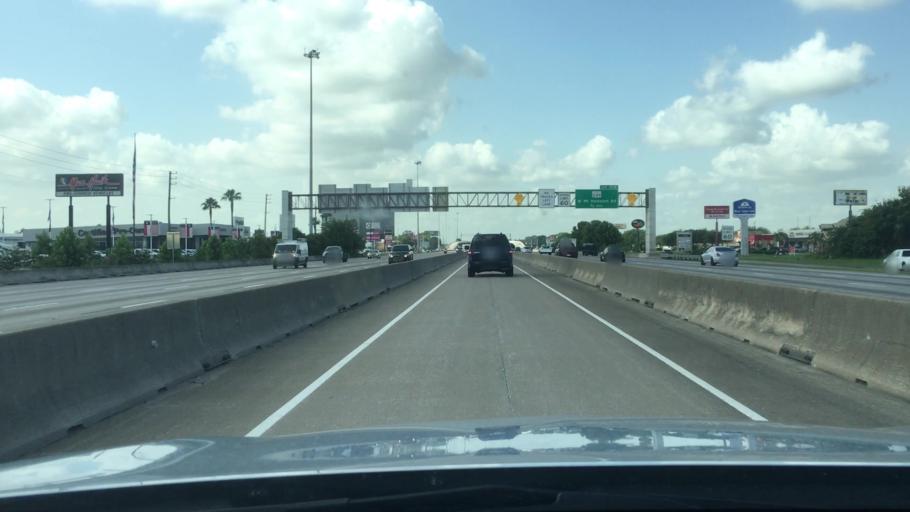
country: US
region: Texas
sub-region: Harris County
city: Aldine
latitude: 29.9278
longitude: -95.4120
